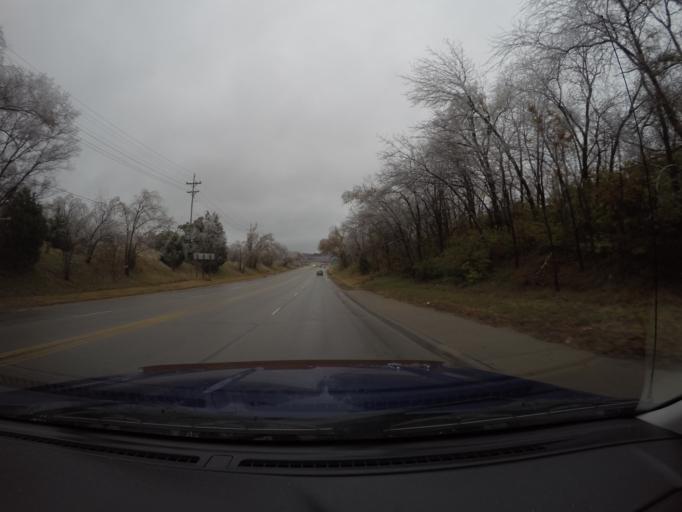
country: US
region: Kansas
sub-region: Riley County
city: Manhattan
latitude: 39.1725
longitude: -96.5923
